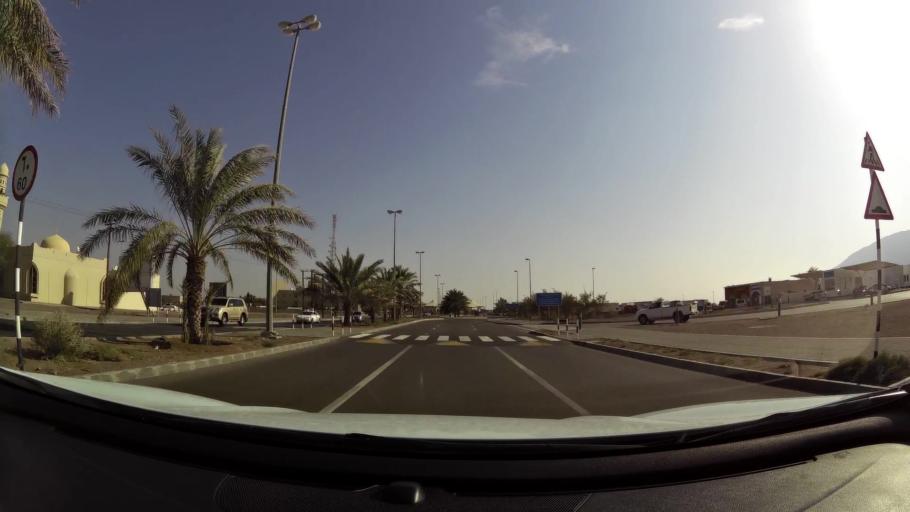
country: AE
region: Abu Dhabi
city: Al Ain
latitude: 24.0301
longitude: 55.8455
